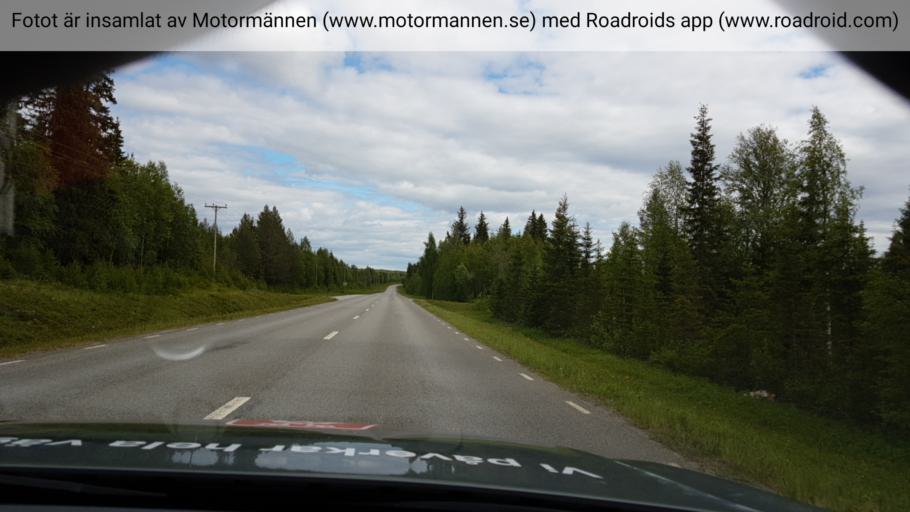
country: SE
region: Jaemtland
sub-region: Stroemsunds Kommun
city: Stroemsund
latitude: 64.2994
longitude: 15.3208
